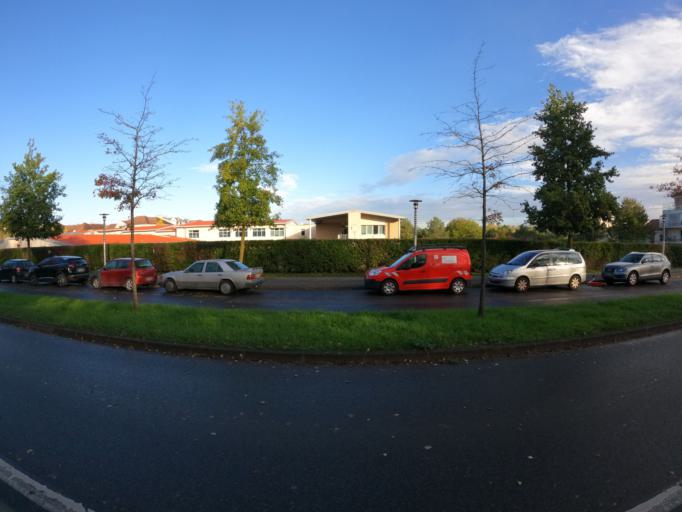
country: FR
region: Ile-de-France
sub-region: Departement de Seine-et-Marne
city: Ferrieres-en-Brie
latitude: 48.8341
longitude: 2.7134
